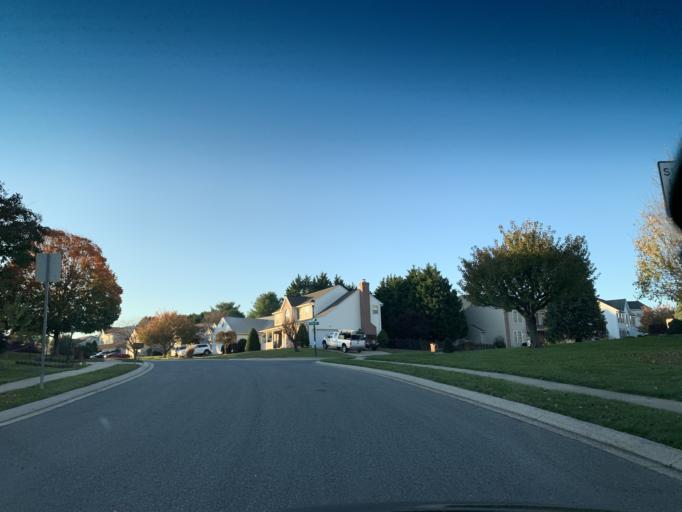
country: US
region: Maryland
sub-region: Harford County
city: Bel Air North
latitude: 39.5639
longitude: -76.3805
